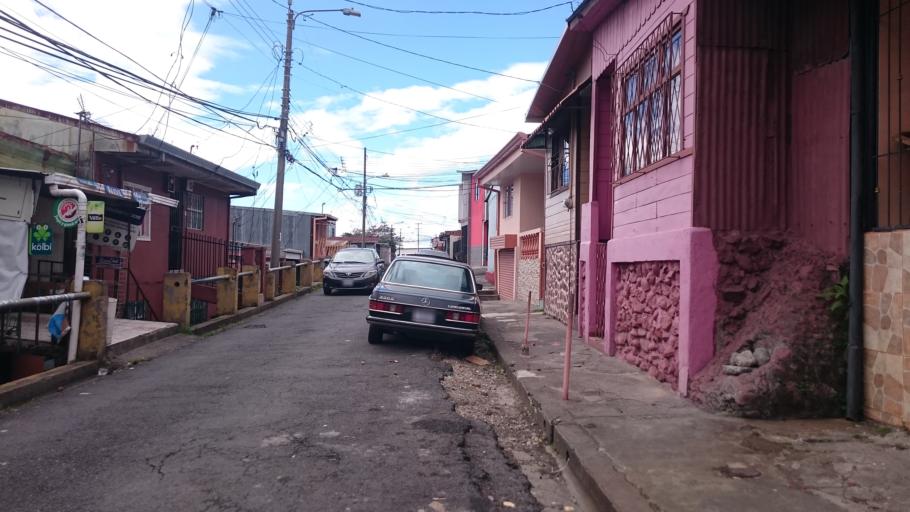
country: CR
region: San Jose
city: Calle Blancos
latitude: 9.9433
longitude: -84.0702
